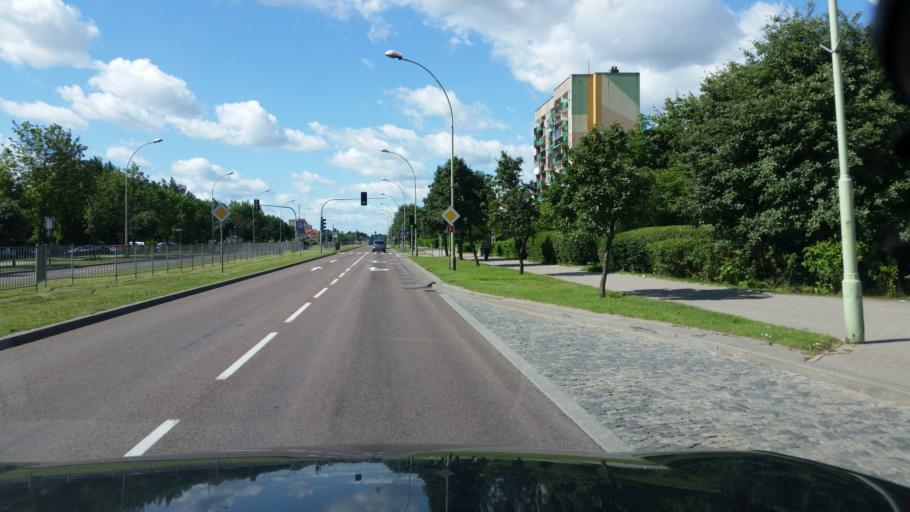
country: PL
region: Podlasie
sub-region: Suwalki
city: Suwalki
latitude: 54.1232
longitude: 22.9423
